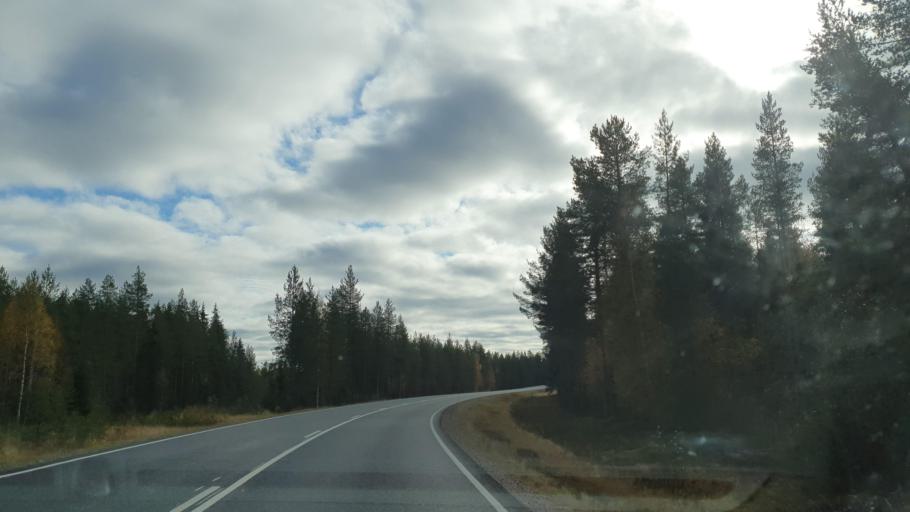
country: FI
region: Northern Ostrobothnia
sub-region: Oulunkaari
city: Pudasjaervi
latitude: 65.3516
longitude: 27.3923
